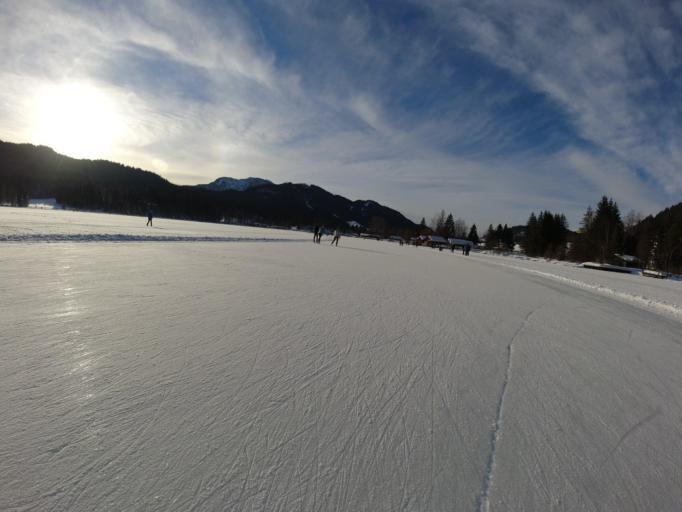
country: AT
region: Carinthia
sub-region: Politischer Bezirk Spittal an der Drau
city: Steinfeld
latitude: 46.7205
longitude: 13.2714
